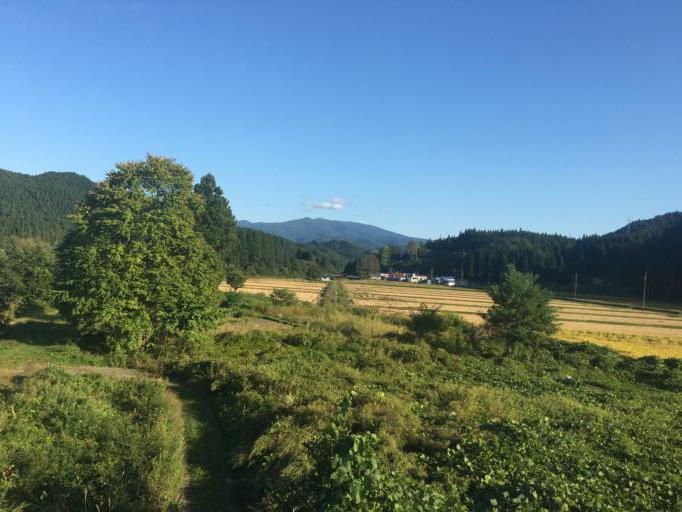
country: JP
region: Akita
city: Takanosu
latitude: 40.0560
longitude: 140.4153
